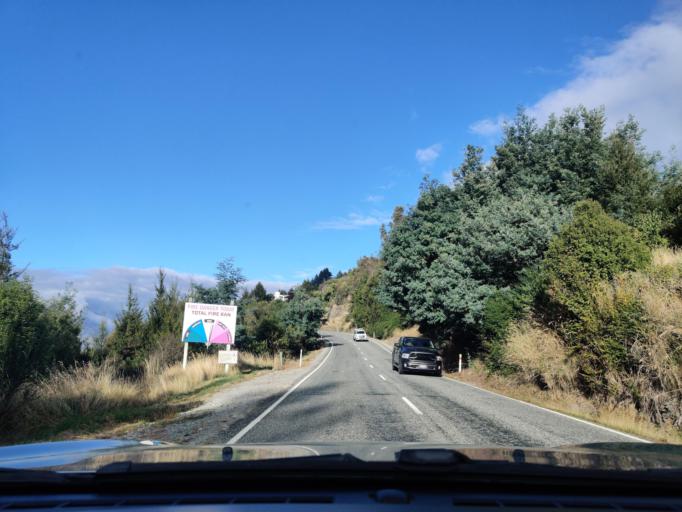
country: NZ
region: Otago
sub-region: Queenstown-Lakes District
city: Queenstown
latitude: -45.0406
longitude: 168.6380
